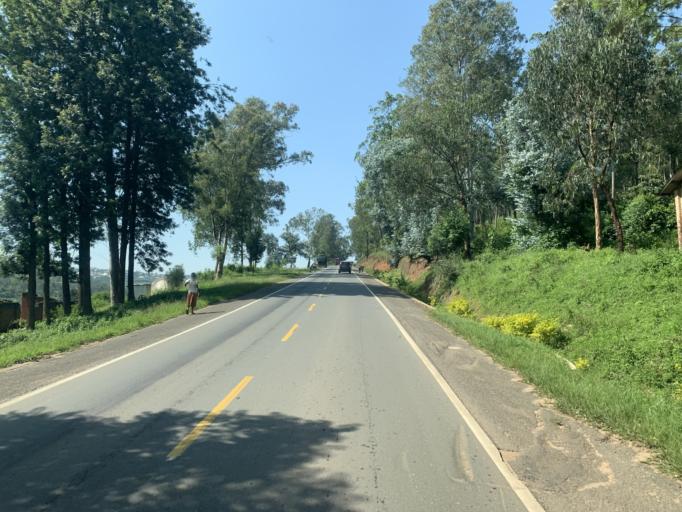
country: RW
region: Kigali
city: Kigali
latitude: -1.9912
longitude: 29.9286
